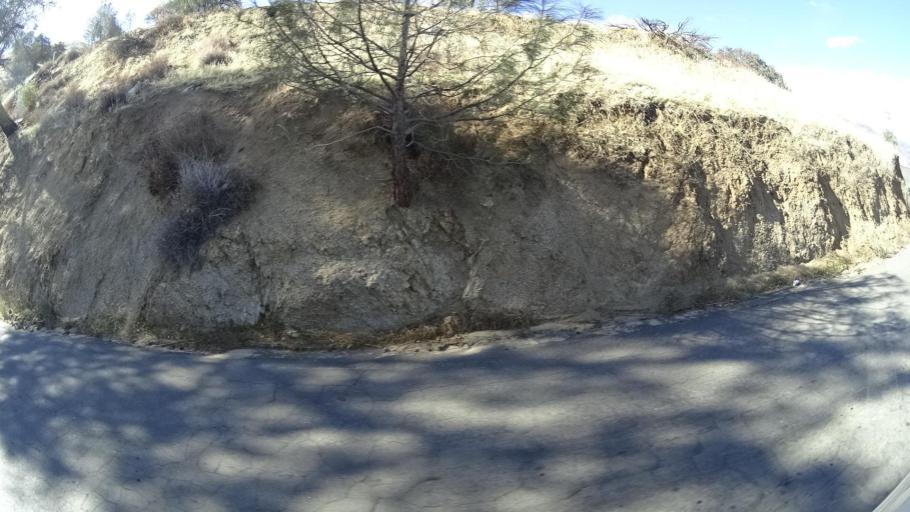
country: US
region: California
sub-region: Kern County
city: Bodfish
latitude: 35.5876
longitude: -118.5007
